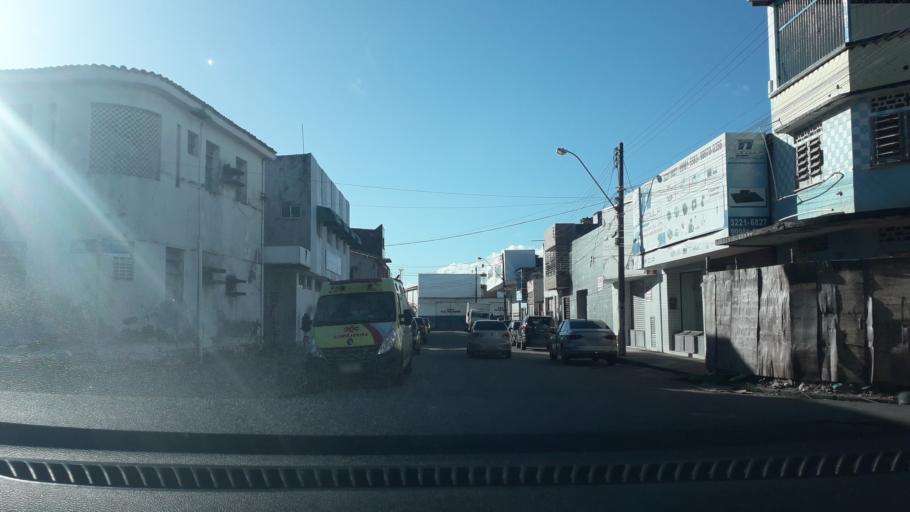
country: BR
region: Alagoas
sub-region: Maceio
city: Maceio
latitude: -9.6625
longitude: -35.7455
